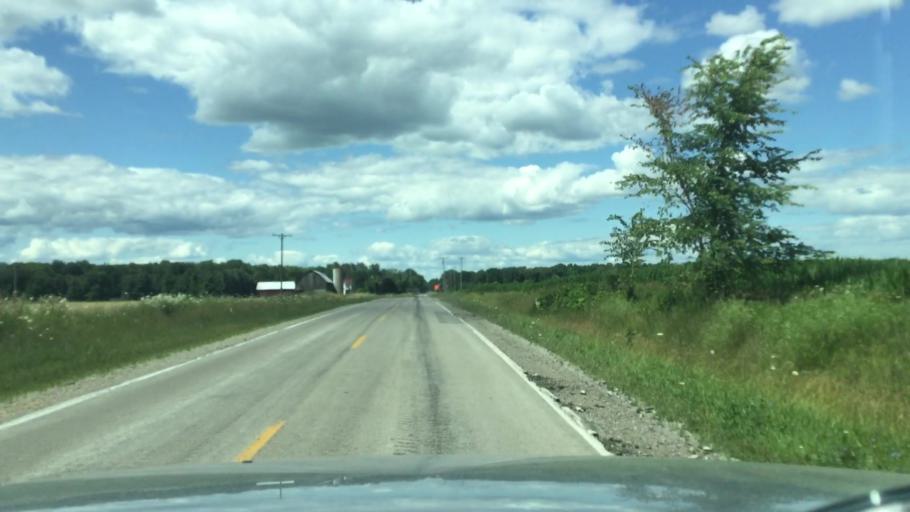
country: US
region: Michigan
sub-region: Saginaw County
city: Hemlock
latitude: 43.3614
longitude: -84.1903
